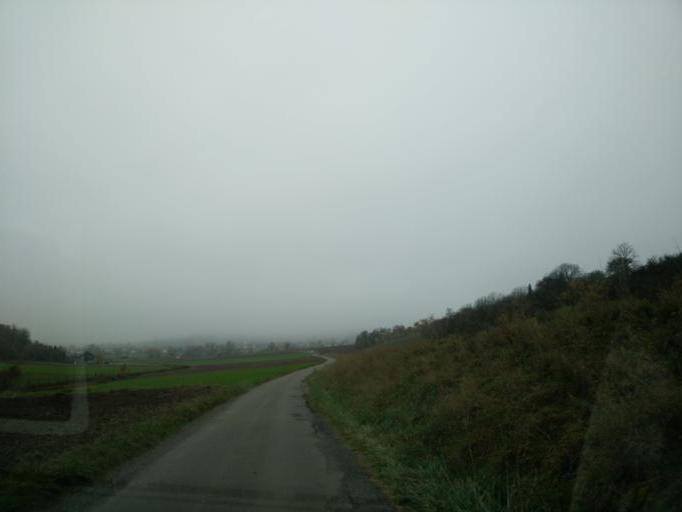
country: DE
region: Baden-Wuerttemberg
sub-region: Tuebingen Region
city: Rottenburg
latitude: 48.5334
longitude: 8.9773
